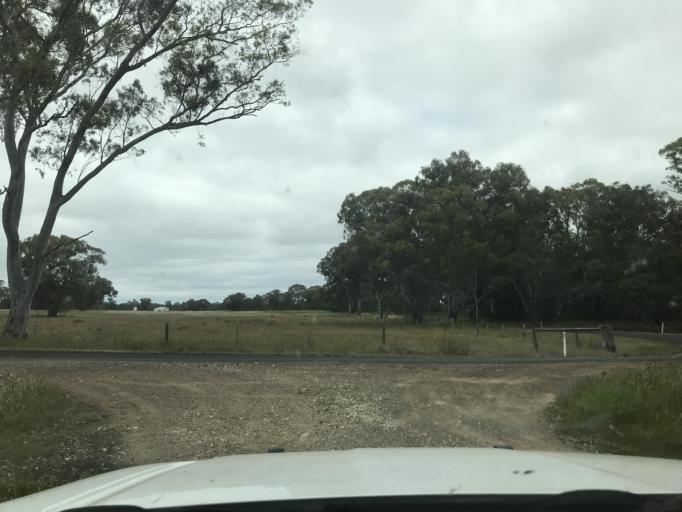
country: AU
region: South Australia
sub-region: Wattle Range
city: Penola
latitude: -37.1996
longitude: 140.9717
